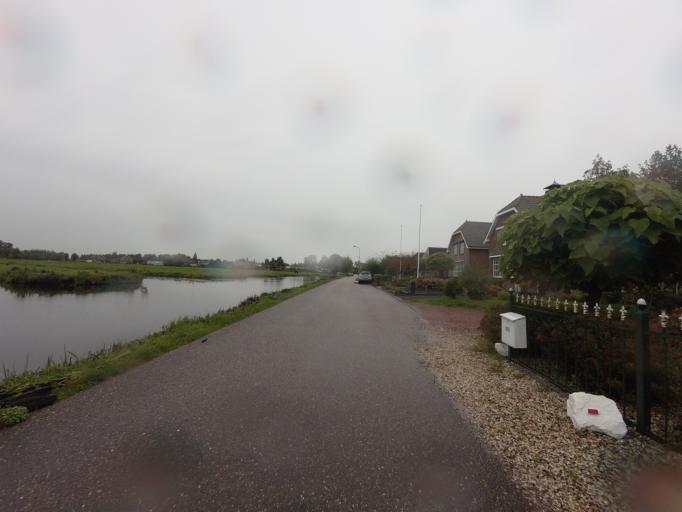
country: NL
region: South Holland
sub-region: Molenwaard
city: Liesveld
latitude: 51.8877
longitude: 4.8518
